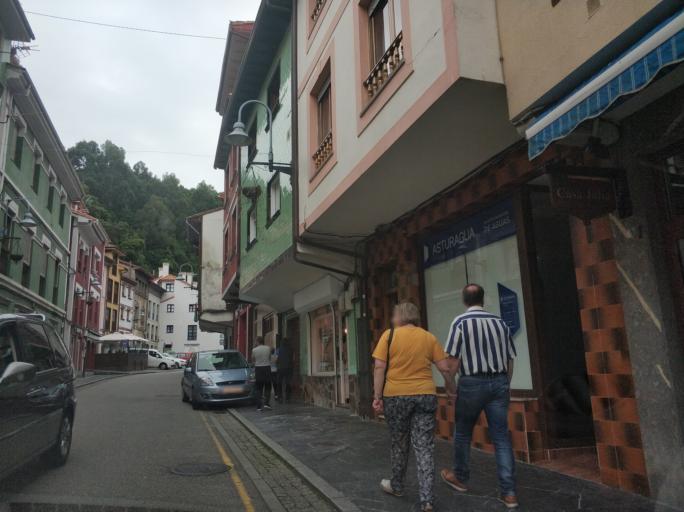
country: ES
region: Asturias
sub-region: Province of Asturias
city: Cudillero
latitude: 43.5625
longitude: -6.1465
